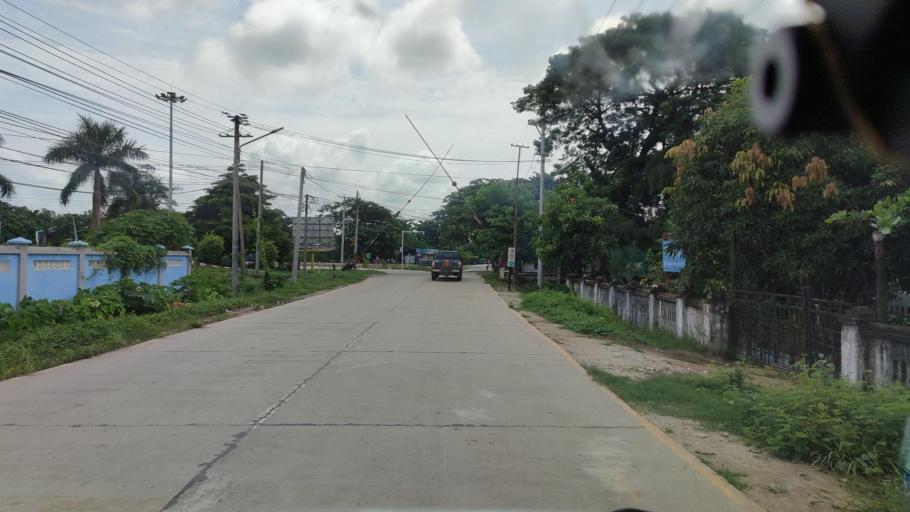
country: MM
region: Bago
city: Taungoo
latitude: 18.9538
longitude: 96.4380
